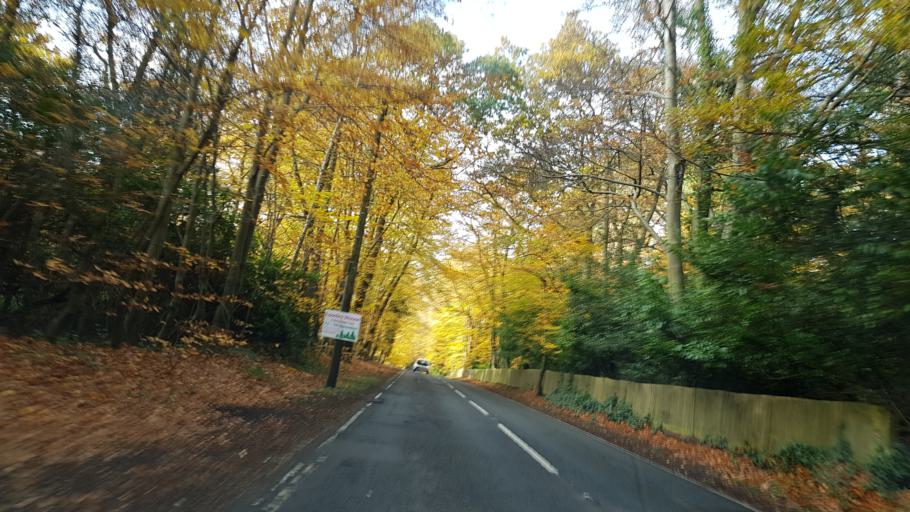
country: GB
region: England
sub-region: Surrey
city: Elstead
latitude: 51.1928
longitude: -0.7311
